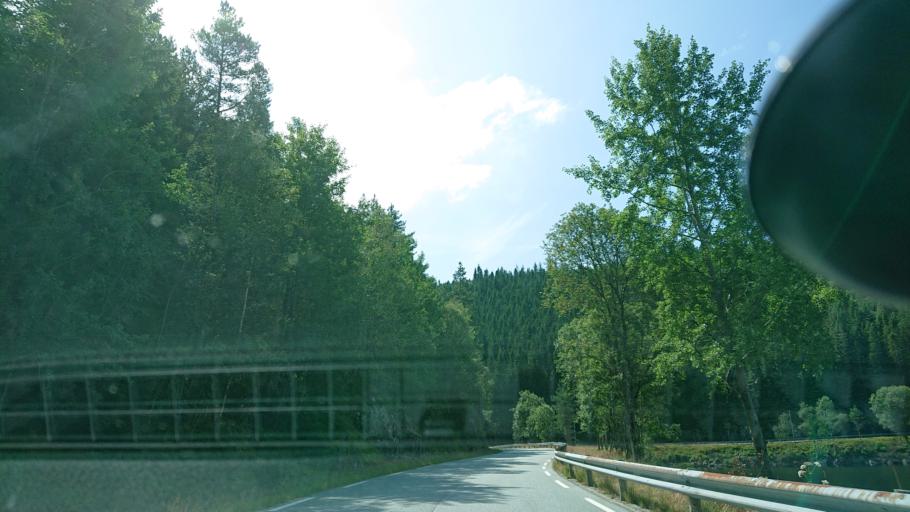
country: NO
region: Rogaland
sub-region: Hjelmeland
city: Hjelmelandsvagen
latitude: 59.2426
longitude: 6.2878
